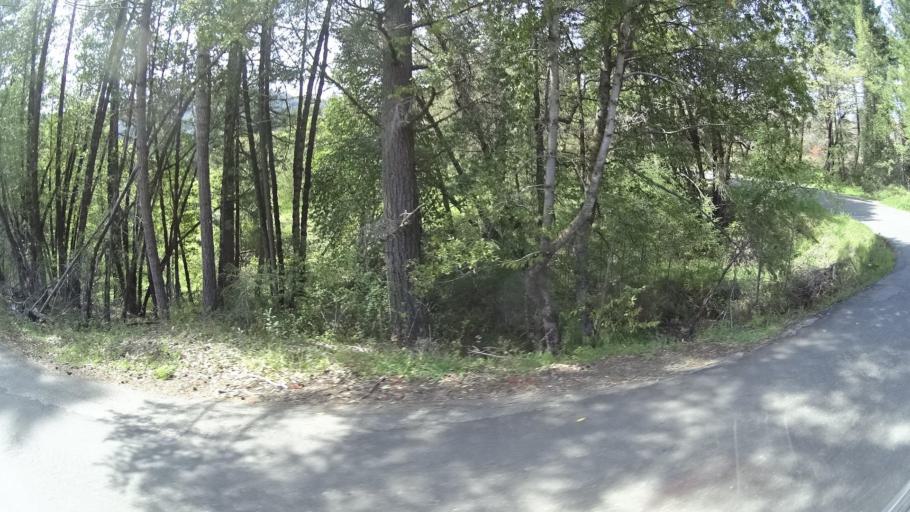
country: US
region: California
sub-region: Humboldt County
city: Redway
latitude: 40.3803
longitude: -123.7423
